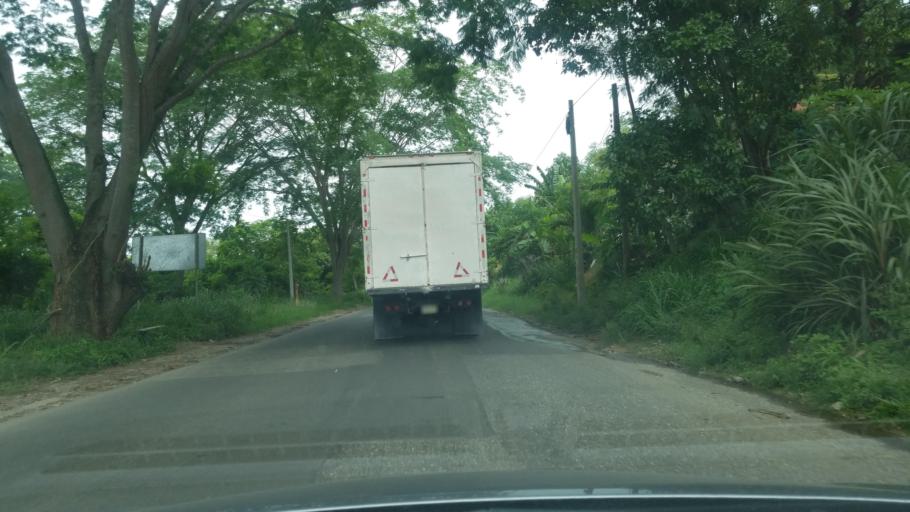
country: HN
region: Santa Barbara
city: San Marcos
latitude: 15.3139
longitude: -88.4339
